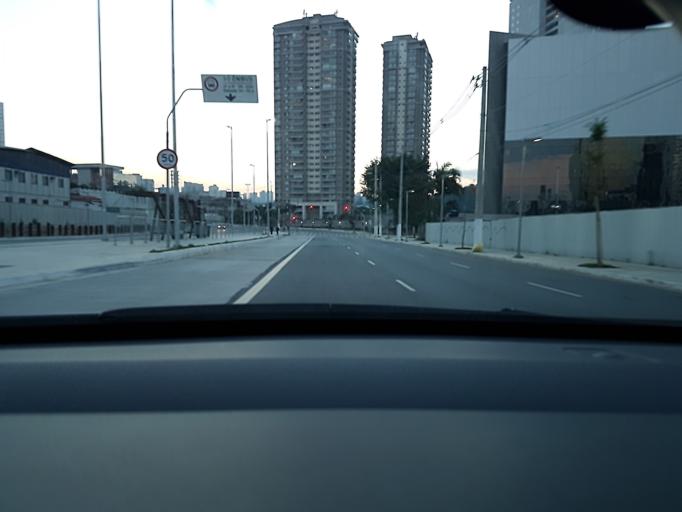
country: BR
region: Sao Paulo
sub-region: Taboao Da Serra
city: Taboao da Serra
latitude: -23.6267
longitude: -46.7047
